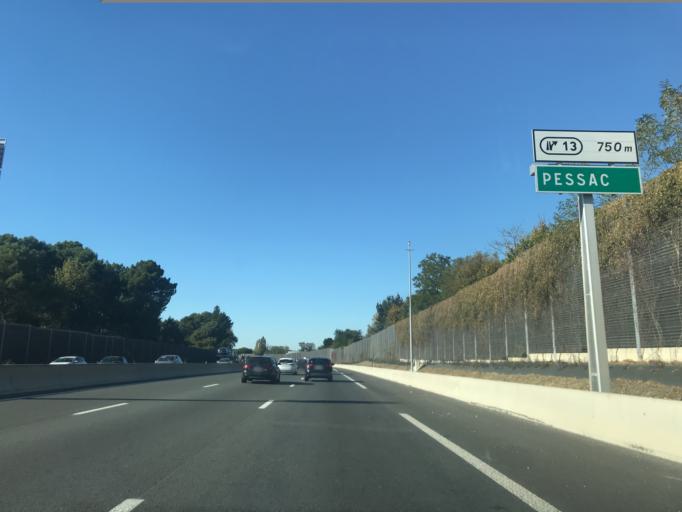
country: FR
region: Aquitaine
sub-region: Departement de la Gironde
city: Pessac
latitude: 44.7966
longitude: -0.6519
